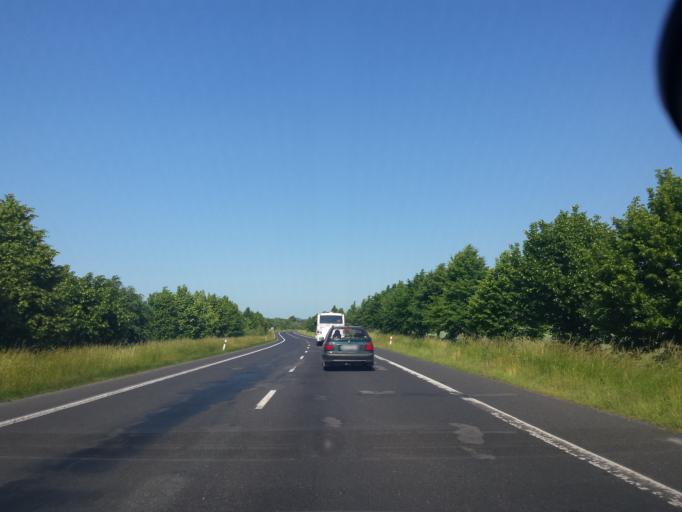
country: CZ
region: Central Bohemia
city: Luzec nad Vltavou
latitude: 50.3453
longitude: 14.4204
